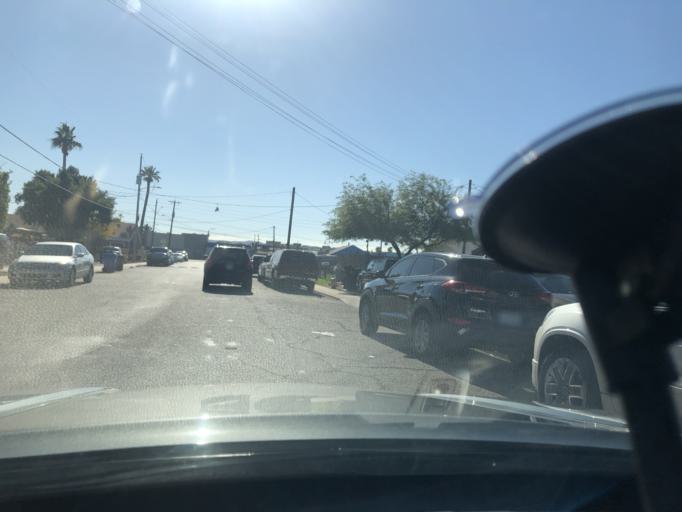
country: US
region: Arizona
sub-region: Maricopa County
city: Phoenix
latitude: 33.4671
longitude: -112.0249
